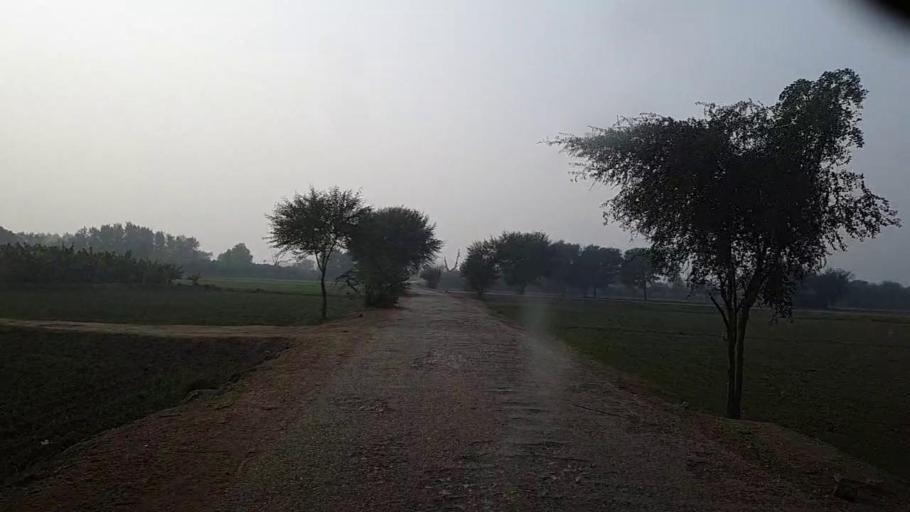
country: PK
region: Sindh
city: Bozdar
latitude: 27.1508
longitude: 68.6632
